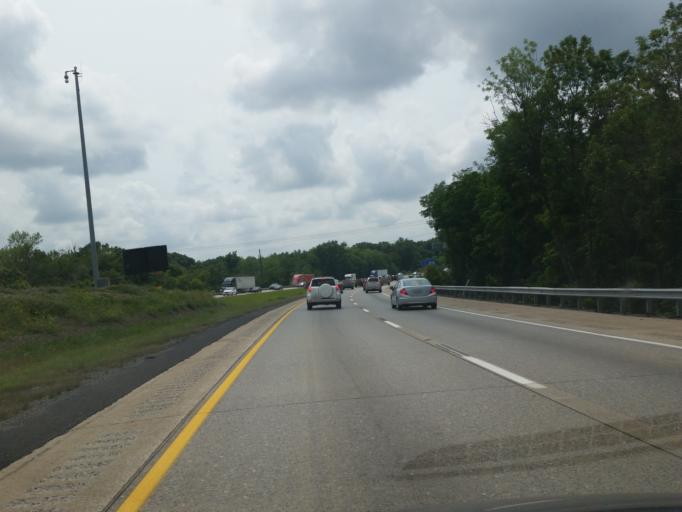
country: US
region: Pennsylvania
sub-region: Dauphin County
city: Linglestown
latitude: 40.3329
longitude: -76.7581
